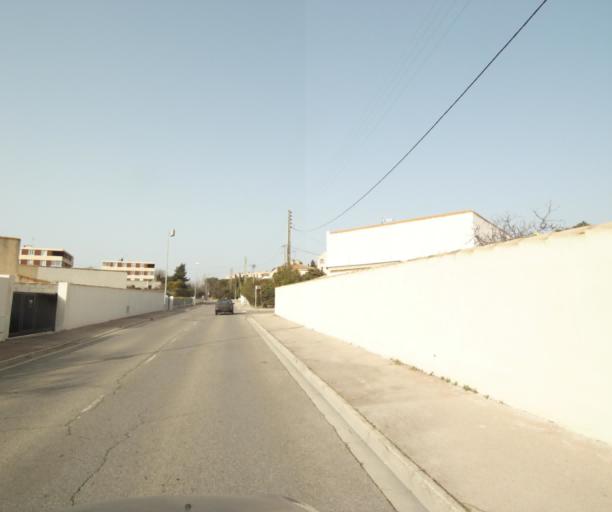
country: FR
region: Provence-Alpes-Cote d'Azur
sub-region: Departement des Bouches-du-Rhone
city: Vitrolles
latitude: 43.4547
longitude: 5.2429
